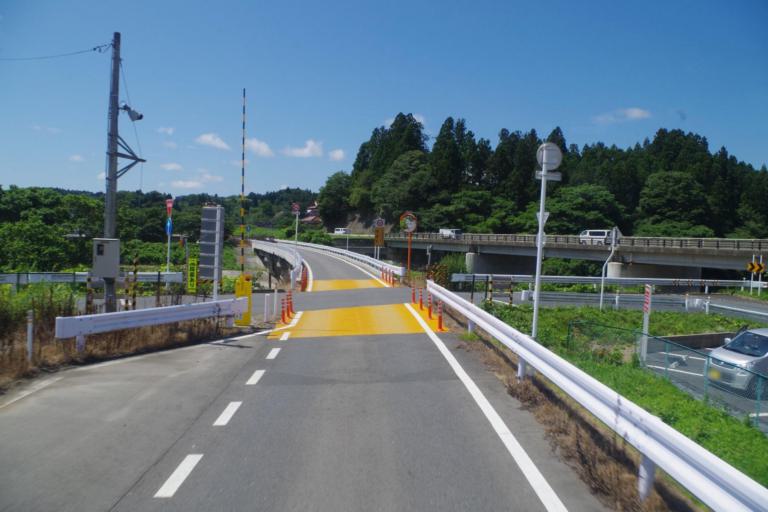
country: JP
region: Iwate
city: Ofunato
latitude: 38.9109
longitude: 141.5483
